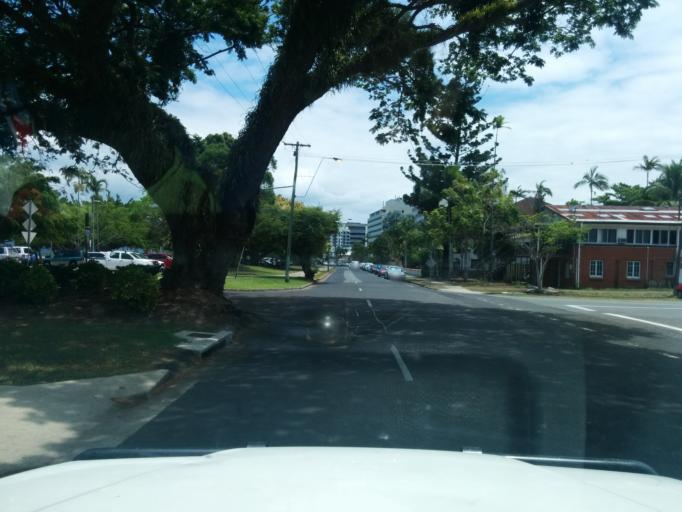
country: AU
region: Queensland
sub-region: Cairns
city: Cairns
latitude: -16.9074
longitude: 145.7643
